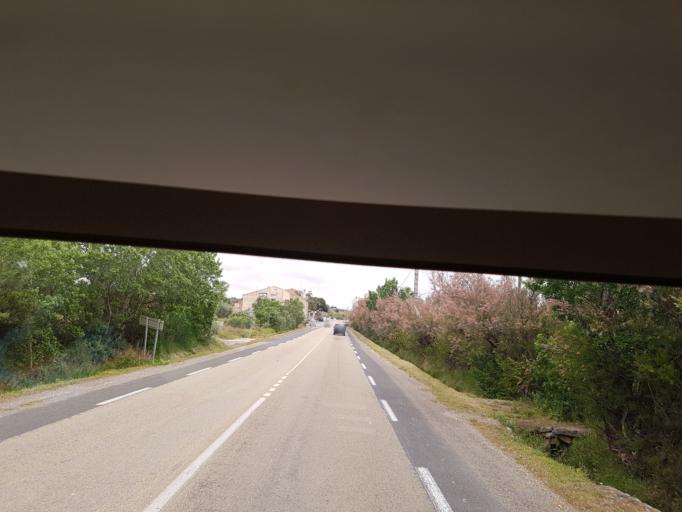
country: FR
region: Languedoc-Roussillon
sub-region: Departement de l'Aude
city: Leucate
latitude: 42.8956
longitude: 2.9977
